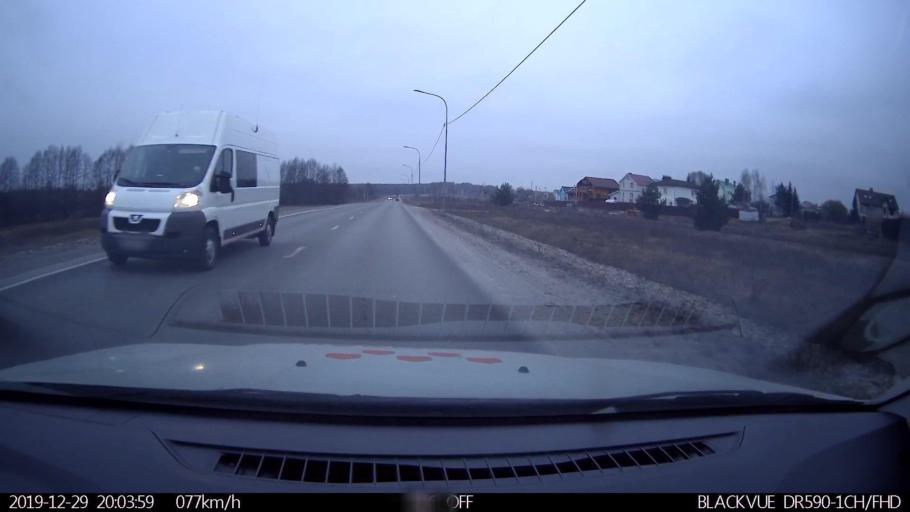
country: RU
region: Nizjnij Novgorod
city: Neklyudovo
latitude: 56.3791
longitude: 44.0115
